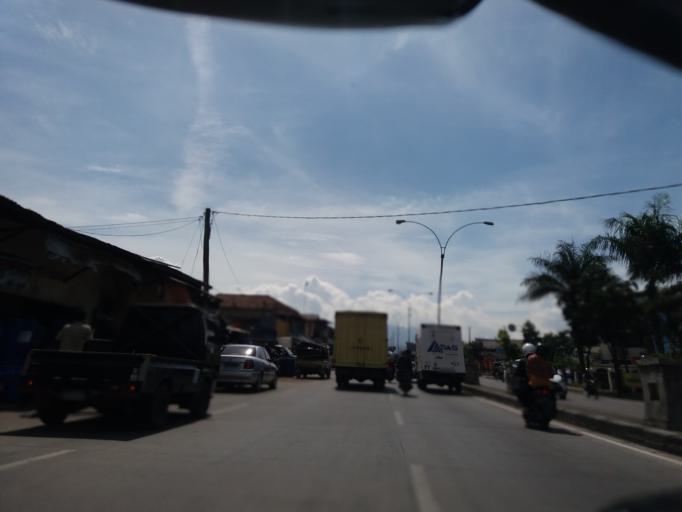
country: ID
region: West Java
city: Margahayukencana
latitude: -6.9265
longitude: 107.5754
